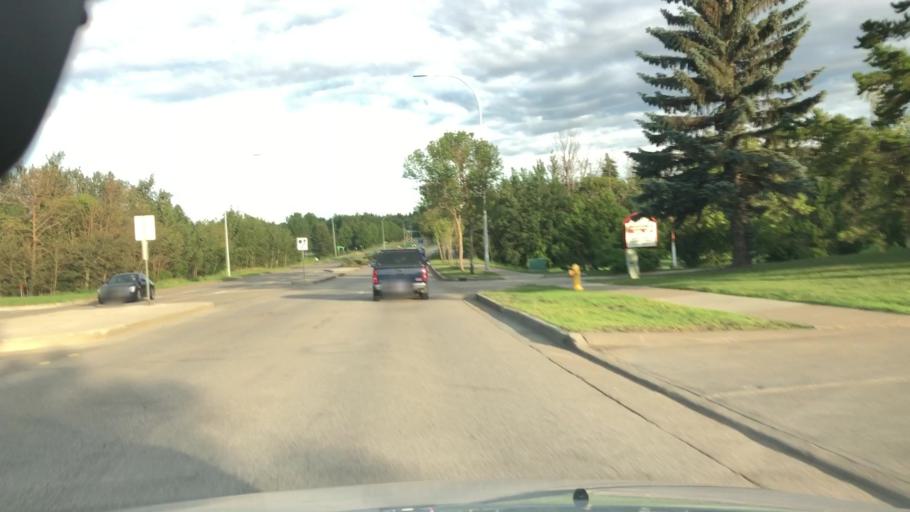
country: CA
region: Alberta
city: St. Albert
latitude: 53.6494
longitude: -113.6167
